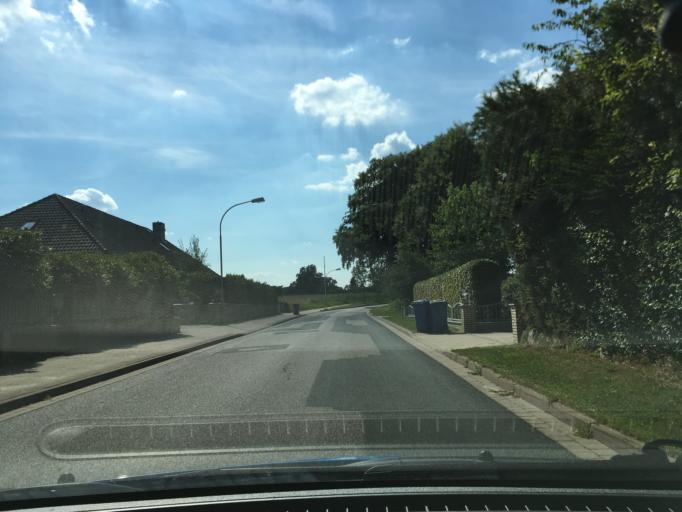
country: DE
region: Lower Saxony
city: Seevetal
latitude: 53.4023
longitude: 9.9213
